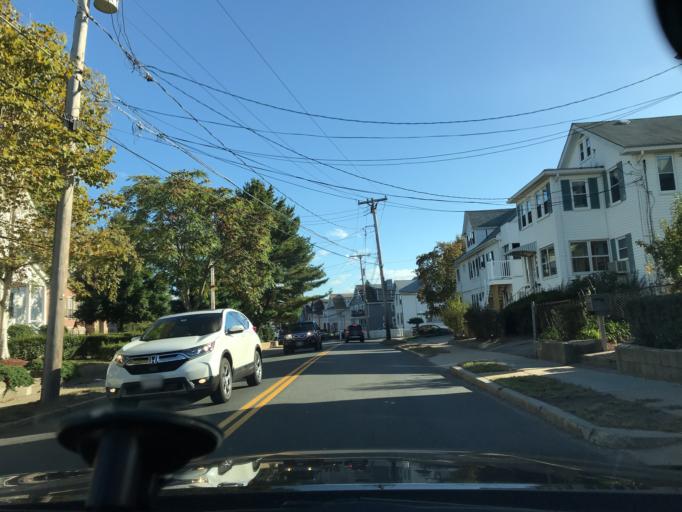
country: US
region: Massachusetts
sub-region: Middlesex County
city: Watertown
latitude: 42.3740
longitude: -71.1580
